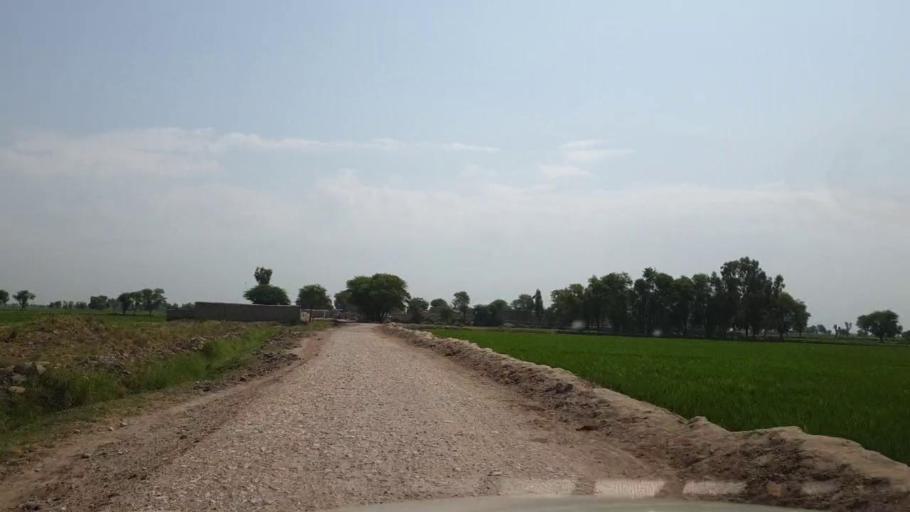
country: PK
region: Sindh
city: Ratodero
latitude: 27.8357
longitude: 68.2848
